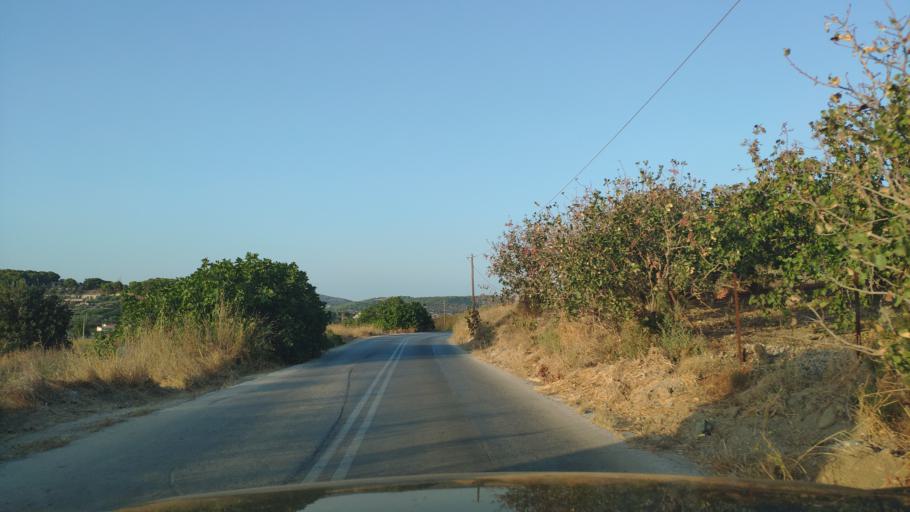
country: GR
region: Attica
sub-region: Nomarchia Anatolikis Attikis
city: Limin Mesoyaias
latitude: 37.9126
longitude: 23.9687
